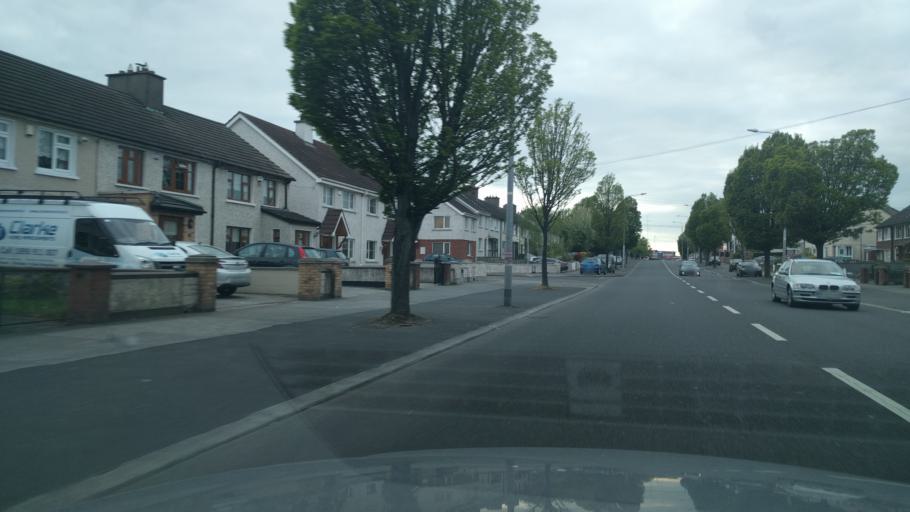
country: IE
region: Leinster
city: Crumlin
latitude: 53.3204
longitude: -6.3380
